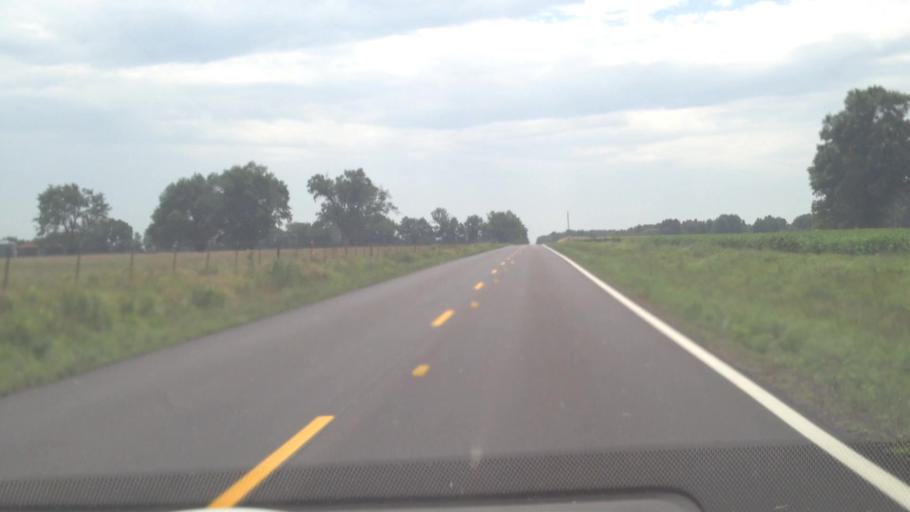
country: US
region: Kansas
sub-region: Crawford County
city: Girard
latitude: 37.5314
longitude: -94.9606
